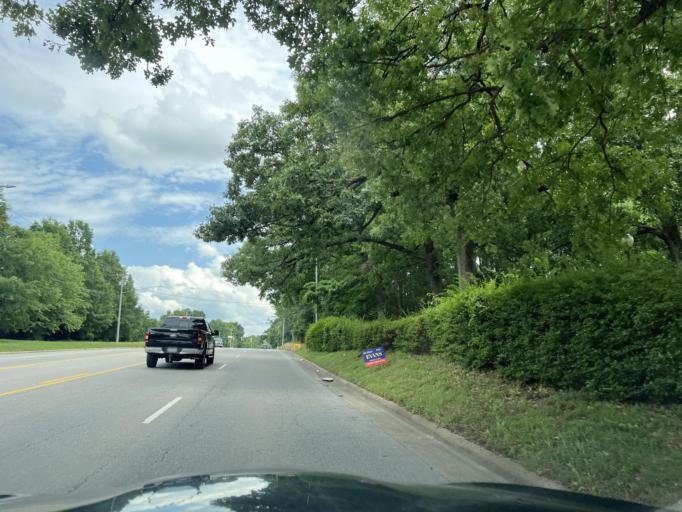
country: US
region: North Carolina
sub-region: Durham County
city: Durham
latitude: 36.0448
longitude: -78.9021
